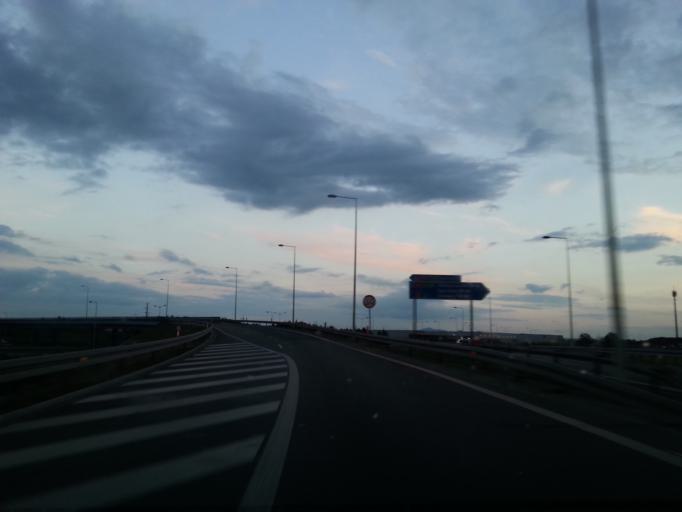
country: PL
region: Lower Silesian Voivodeship
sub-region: Powiat wroclawski
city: Tyniec Maly
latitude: 51.0455
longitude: 16.9315
